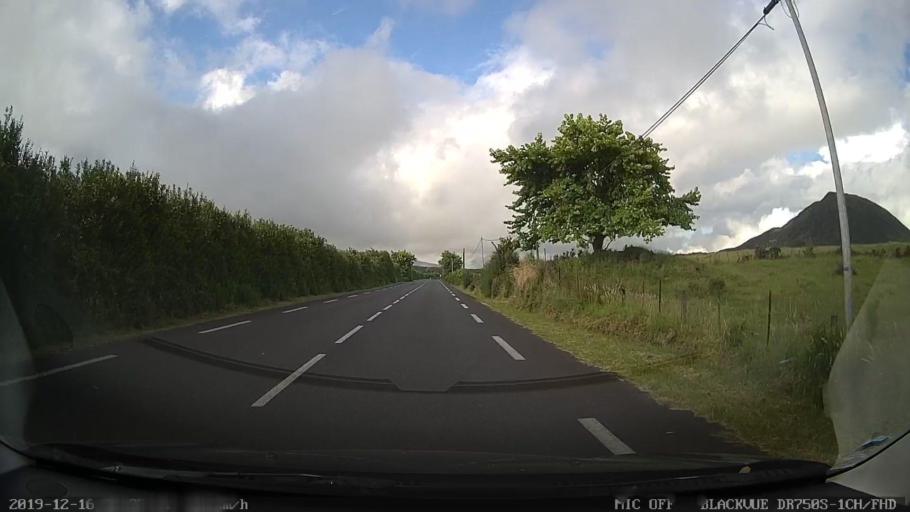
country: RE
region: Reunion
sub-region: Reunion
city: Cilaos
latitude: -21.1821
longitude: 55.5793
